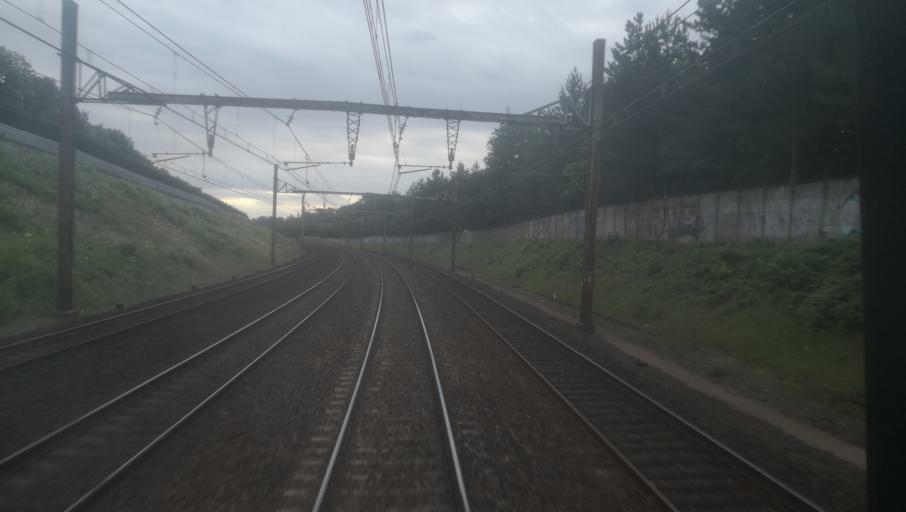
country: FR
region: Ile-de-France
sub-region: Departement de l'Essonne
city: Lardy
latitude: 48.5284
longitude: 2.2797
